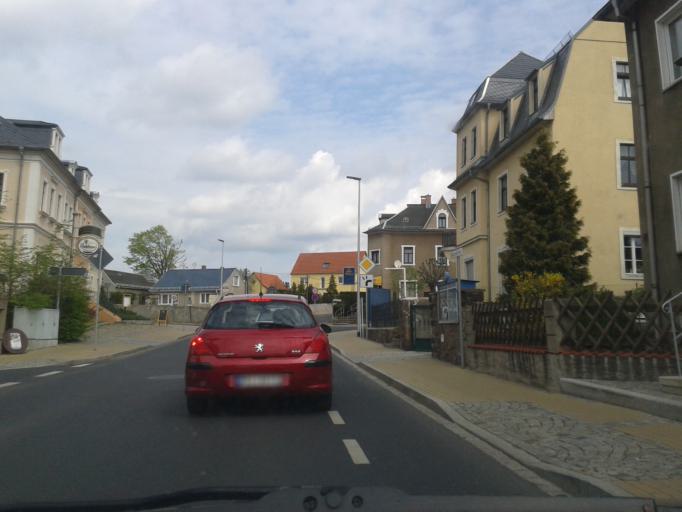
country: DE
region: Saxony
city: Radebeul
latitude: 51.1226
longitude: 13.6318
